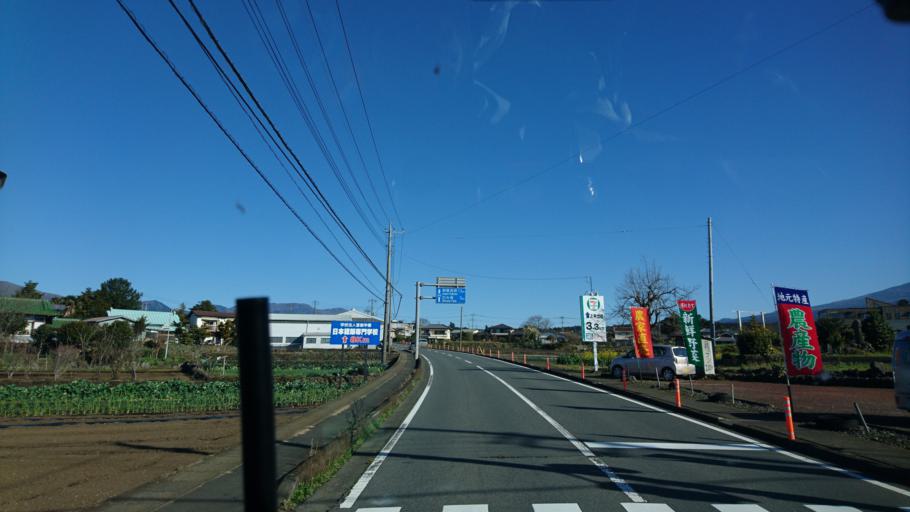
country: JP
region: Shizuoka
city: Fujinomiya
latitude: 35.2782
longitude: 138.6047
